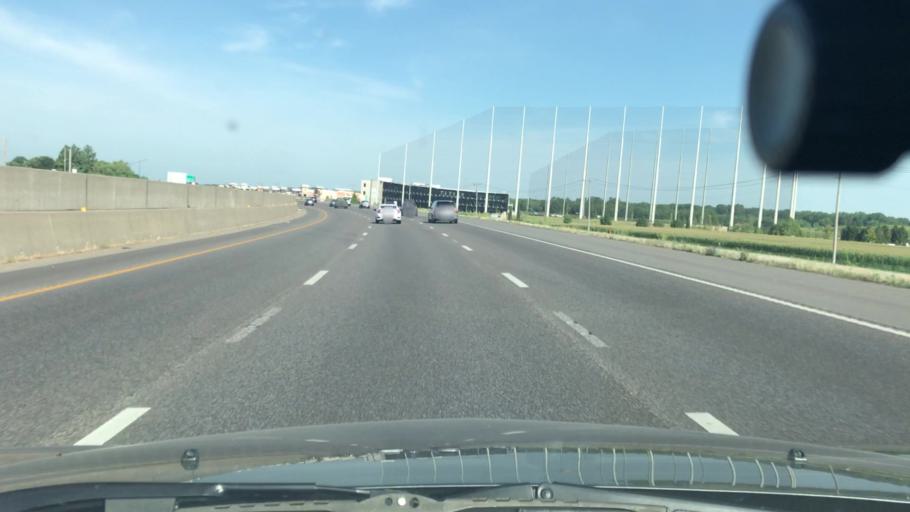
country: US
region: Missouri
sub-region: Saint Louis County
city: Chesterfield
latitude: 38.6685
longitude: -90.5776
